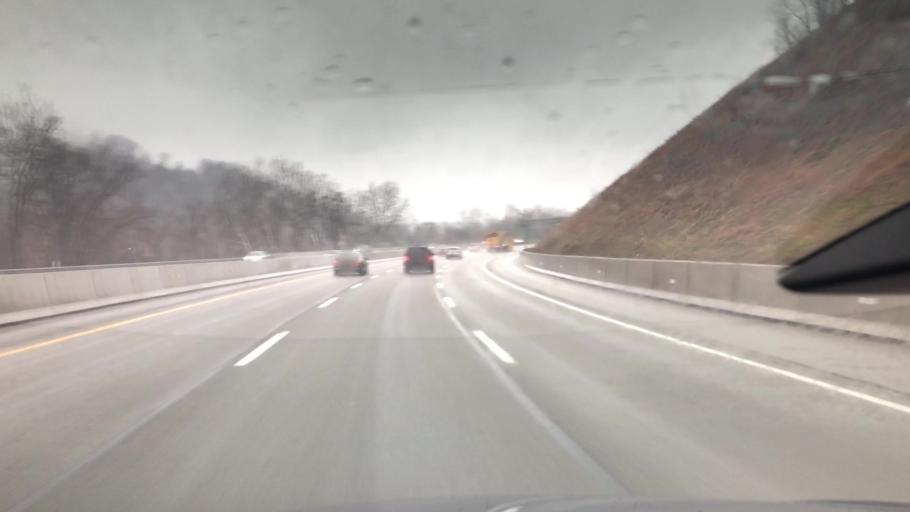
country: US
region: Pennsylvania
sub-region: Allegheny County
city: Oakmont
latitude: 40.5549
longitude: -79.8457
